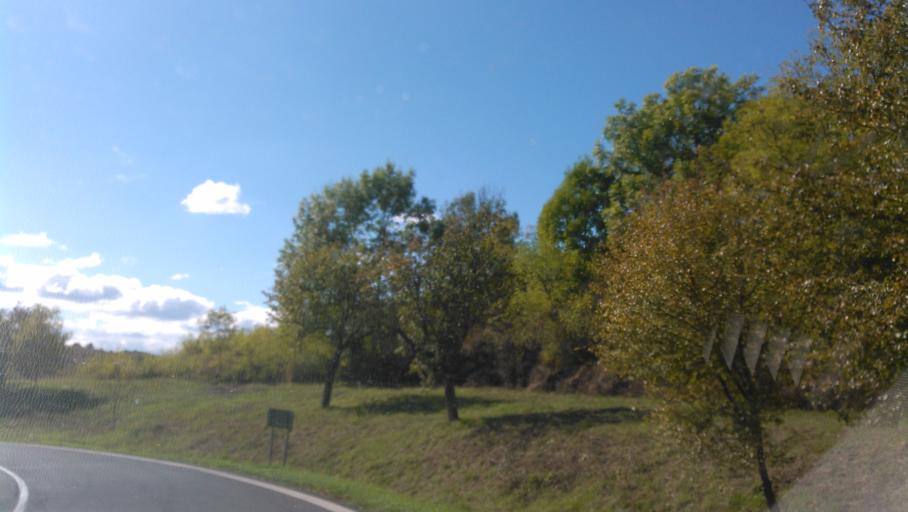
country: SK
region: Banskobystricky
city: Rimavska Sobota
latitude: 48.3791
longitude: 19.9084
